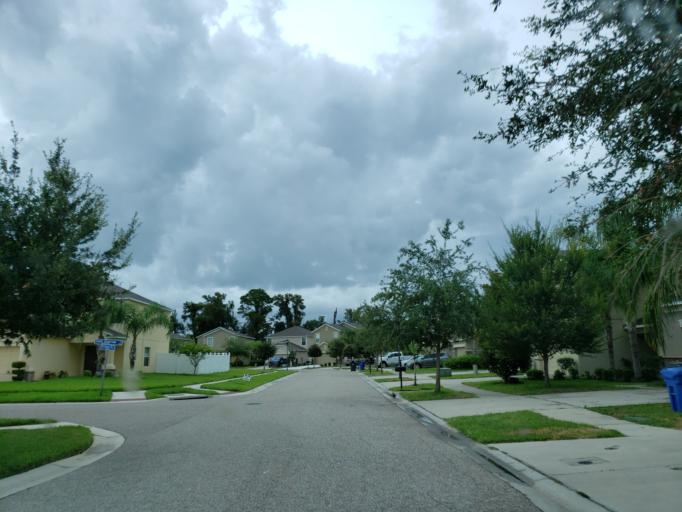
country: US
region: Florida
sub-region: Hillsborough County
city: Ruskin
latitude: 27.7301
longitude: -82.4048
